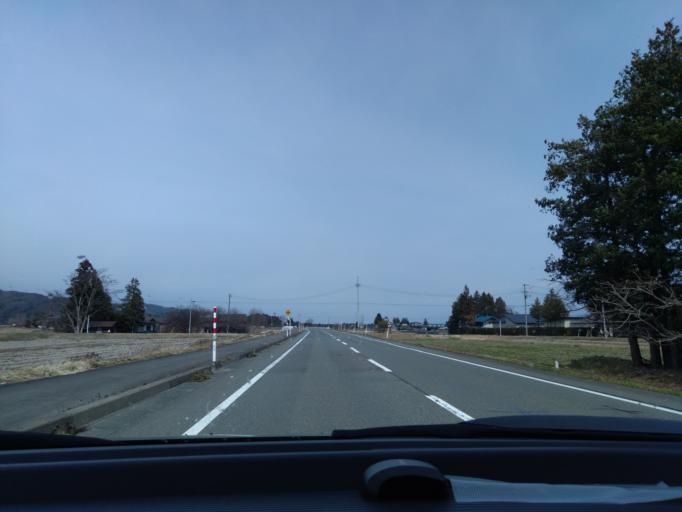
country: JP
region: Iwate
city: Morioka-shi
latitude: 39.5738
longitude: 141.1097
